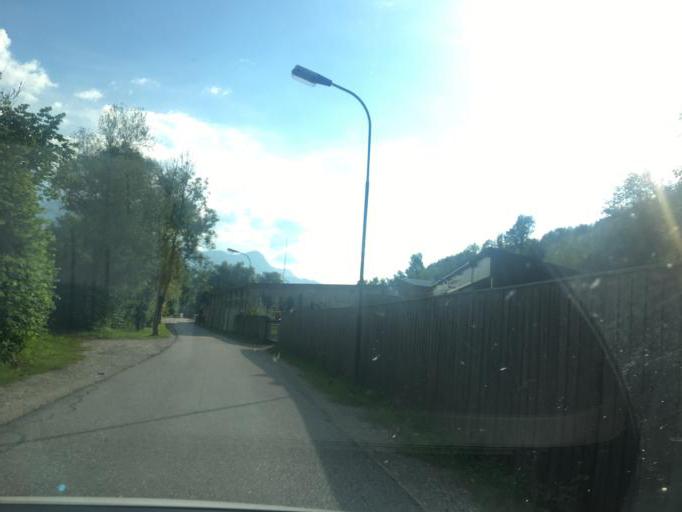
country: AT
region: Styria
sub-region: Politischer Bezirk Liezen
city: Schladming
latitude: 47.3968
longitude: 13.7009
